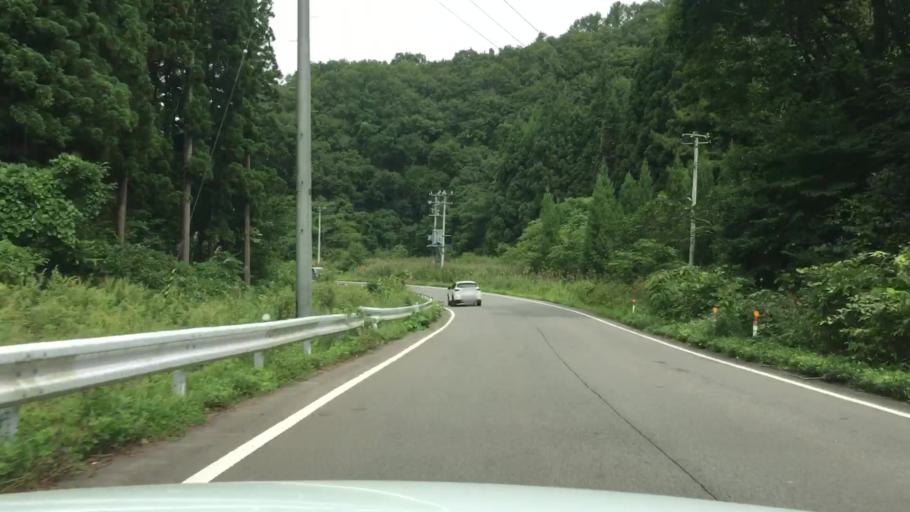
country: JP
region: Aomori
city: Shimokizukuri
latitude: 40.7307
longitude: 140.2519
